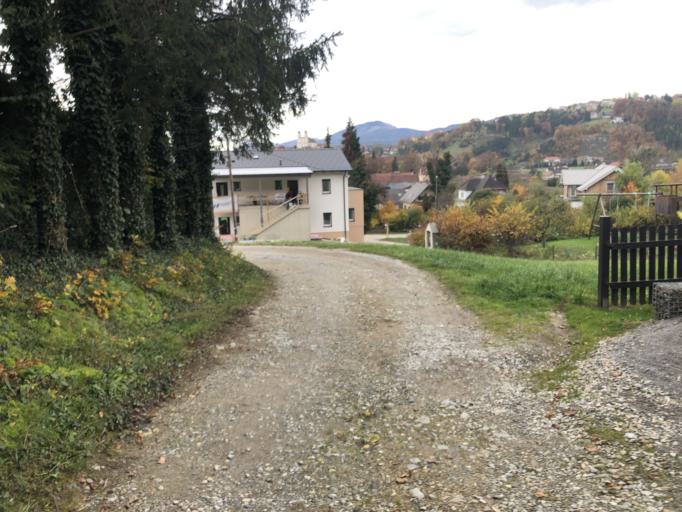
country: AT
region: Styria
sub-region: Politischer Bezirk Weiz
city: Krottendorf
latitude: 47.2278
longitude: 15.6510
